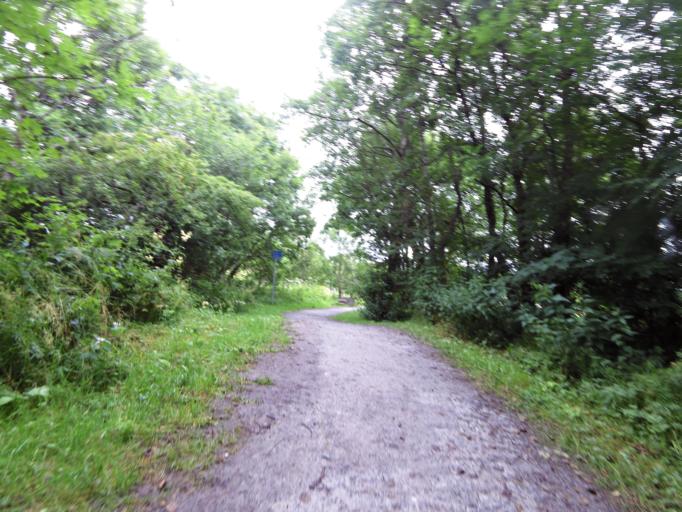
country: GB
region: Scotland
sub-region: Highland
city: Fort William
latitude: 56.8280
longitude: -5.0948
